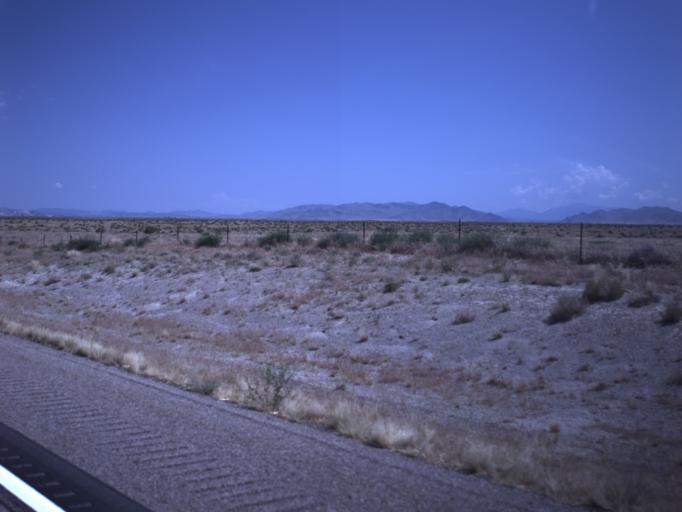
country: US
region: Utah
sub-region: Millard County
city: Delta
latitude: 39.3765
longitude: -112.4964
